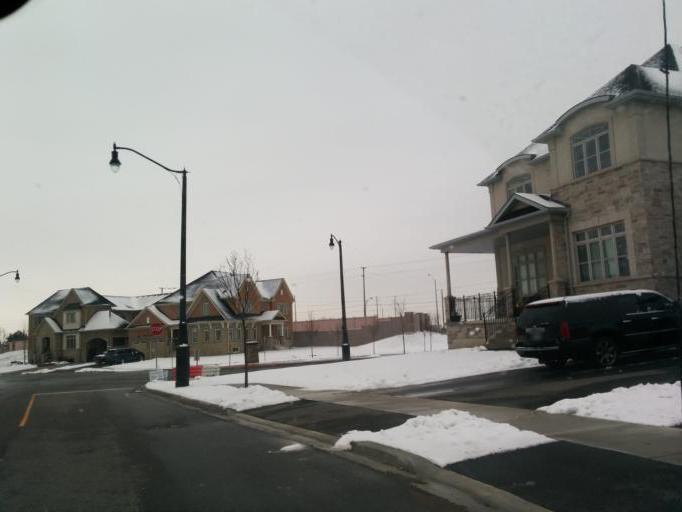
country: CA
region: Ontario
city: Brampton
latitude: 43.7642
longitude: -79.6538
